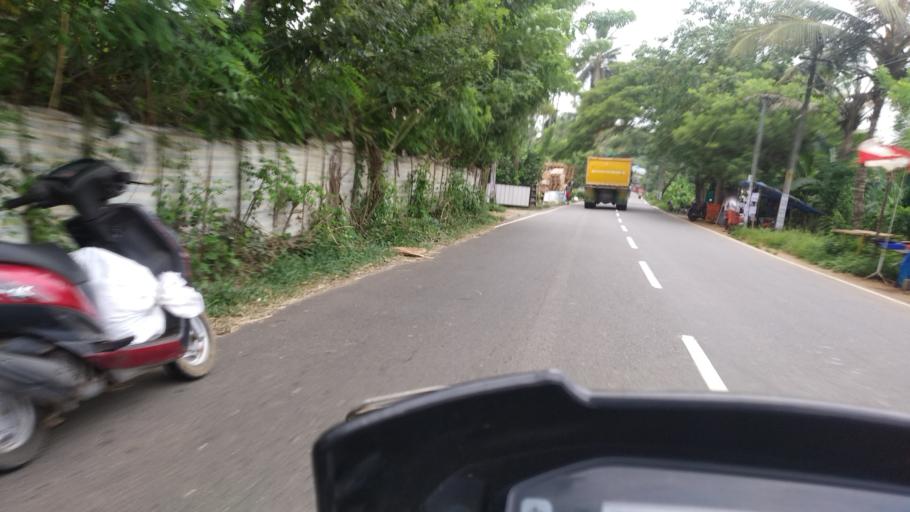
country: IN
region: Kerala
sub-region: Ernakulam
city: Aluva
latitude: 10.1544
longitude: 76.2896
